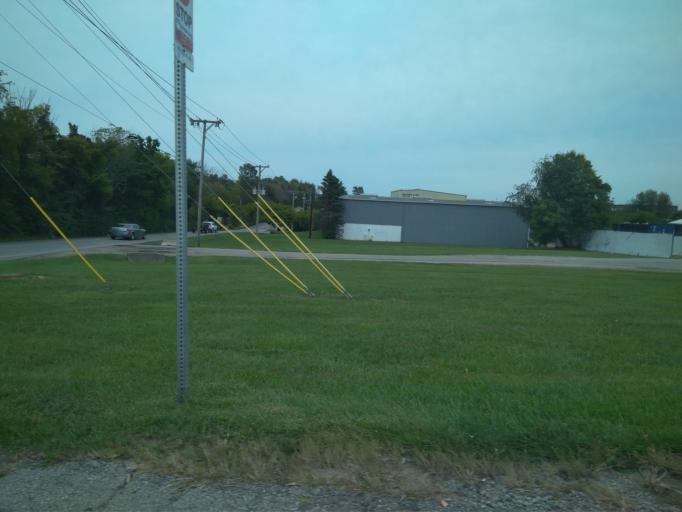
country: US
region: Kentucky
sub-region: Jefferson County
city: Anchorage
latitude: 38.2532
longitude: -85.5134
